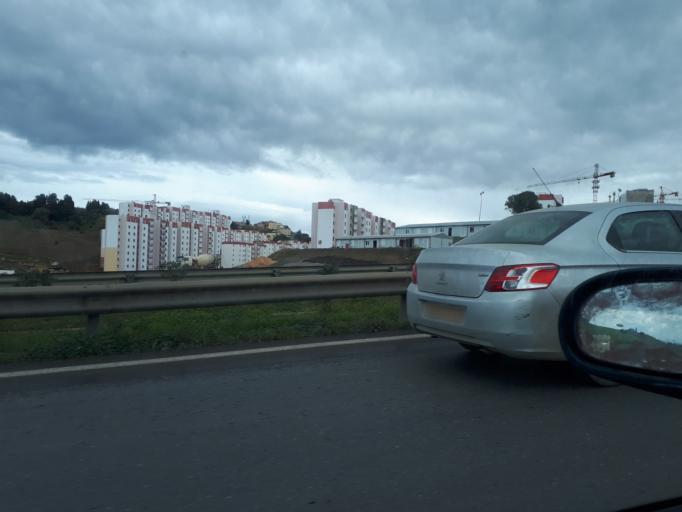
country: DZ
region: Tipaza
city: Douera
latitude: 36.7070
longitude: 2.9324
